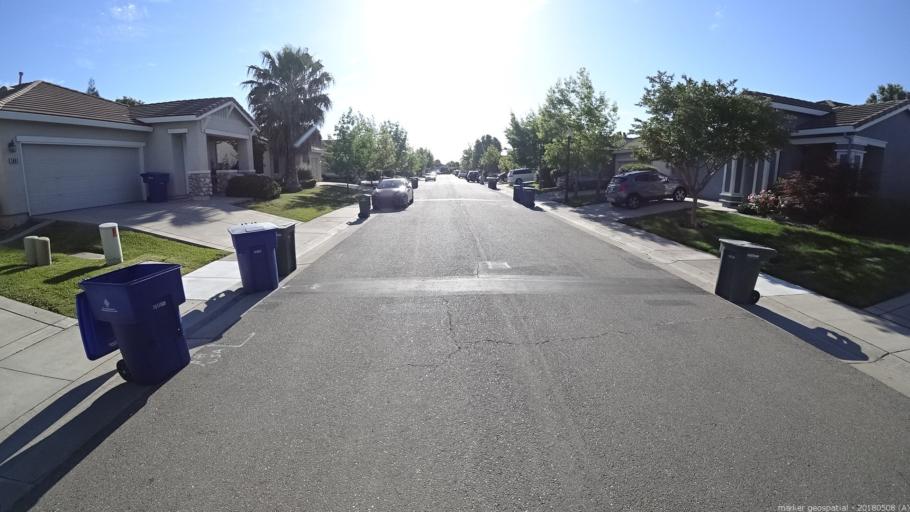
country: US
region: California
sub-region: Sacramento County
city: Elverta
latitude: 38.6827
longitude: -121.5029
